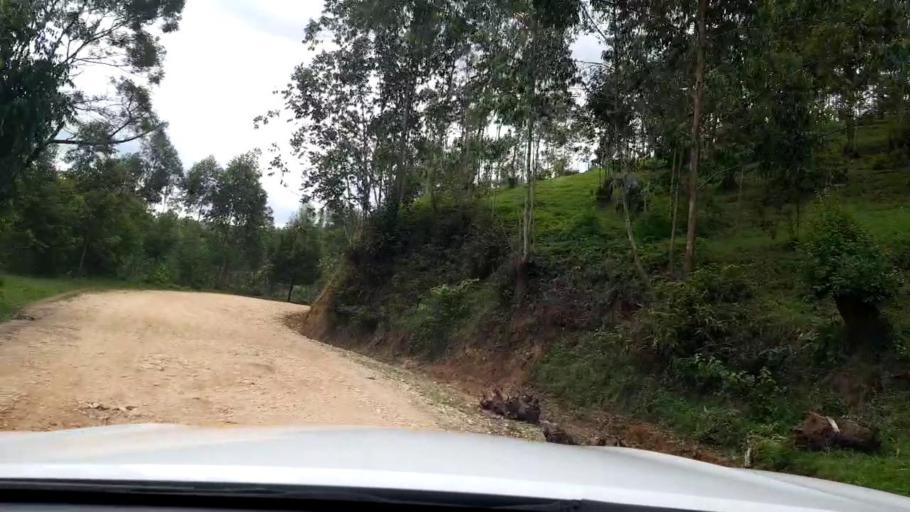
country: RW
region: Southern Province
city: Gitarama
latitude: -1.9383
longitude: 29.6328
